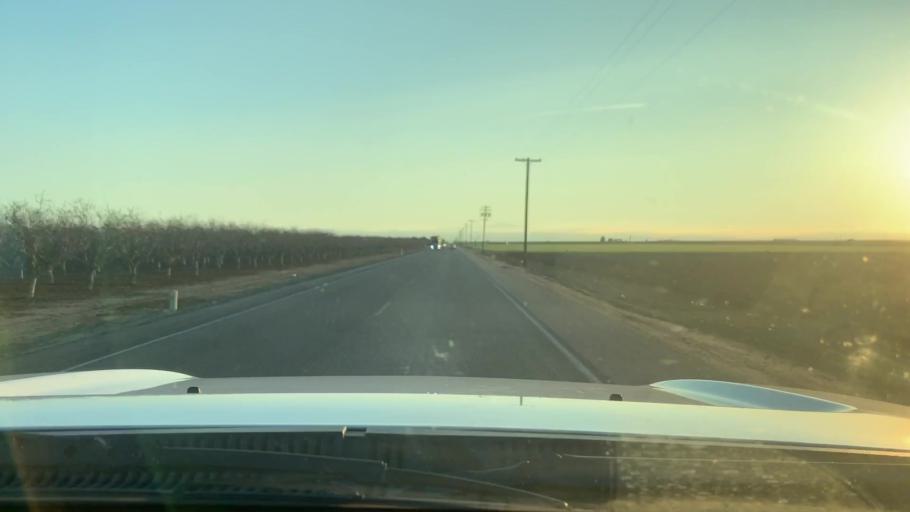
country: US
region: California
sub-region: Kern County
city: Shafter
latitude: 35.5001
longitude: -119.3654
